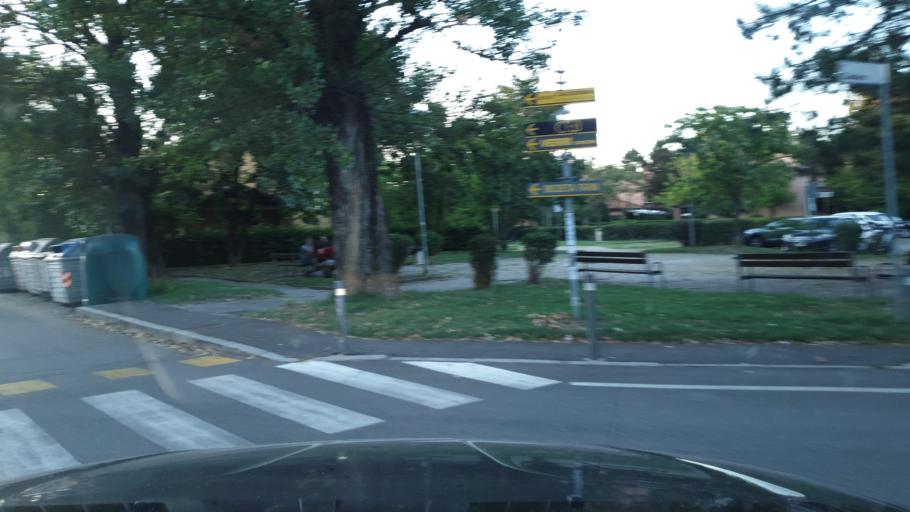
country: IT
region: Emilia-Romagna
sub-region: Provincia di Bologna
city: Quarto Inferiore
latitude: 44.5493
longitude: 11.3993
